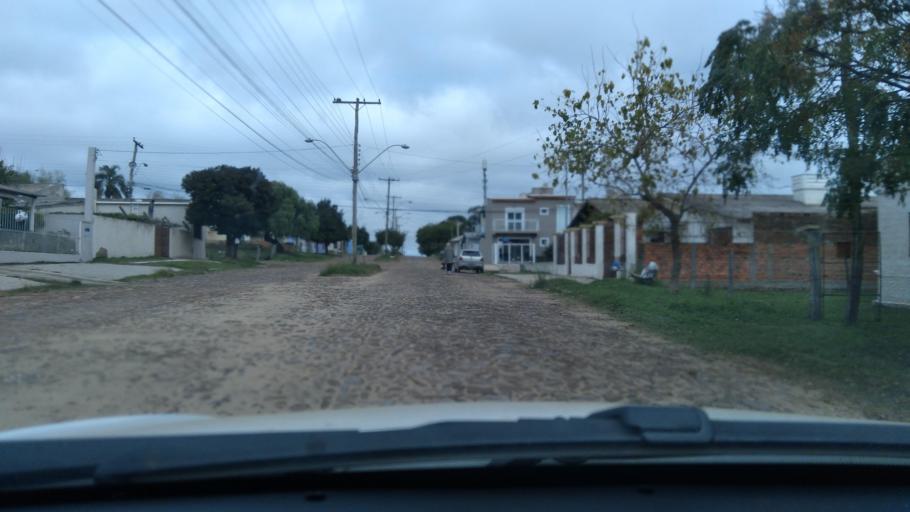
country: BR
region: Rio Grande do Sul
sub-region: Dom Pedrito
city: Dom Pedrito
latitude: -30.9850
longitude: -54.6632
